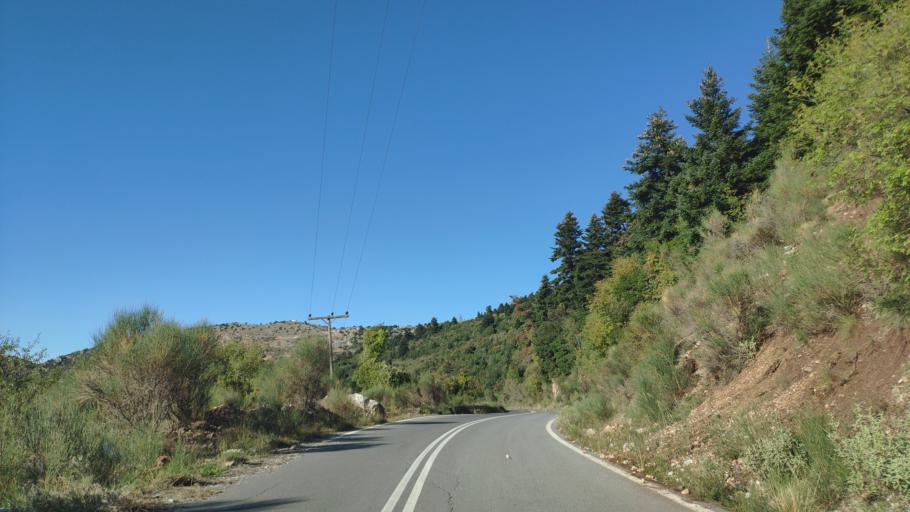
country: GR
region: Peloponnese
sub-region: Nomos Arkadias
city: Dimitsana
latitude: 37.5724
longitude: 22.0617
